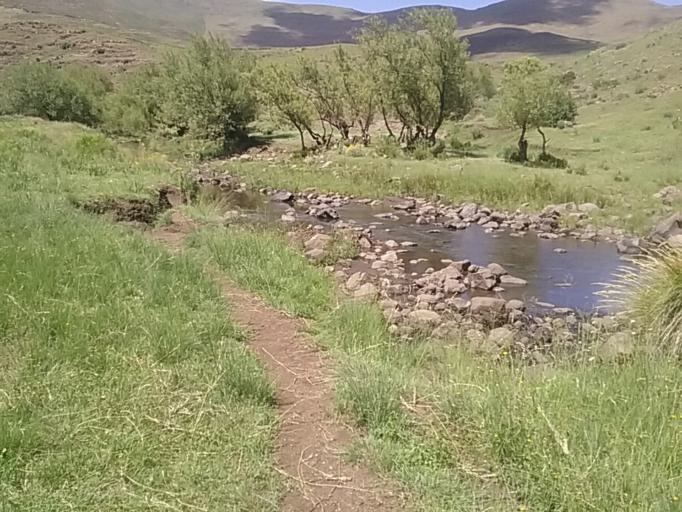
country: LS
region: Qacha's Nek
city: Qacha's Nek
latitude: -30.1654
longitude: 28.2203
